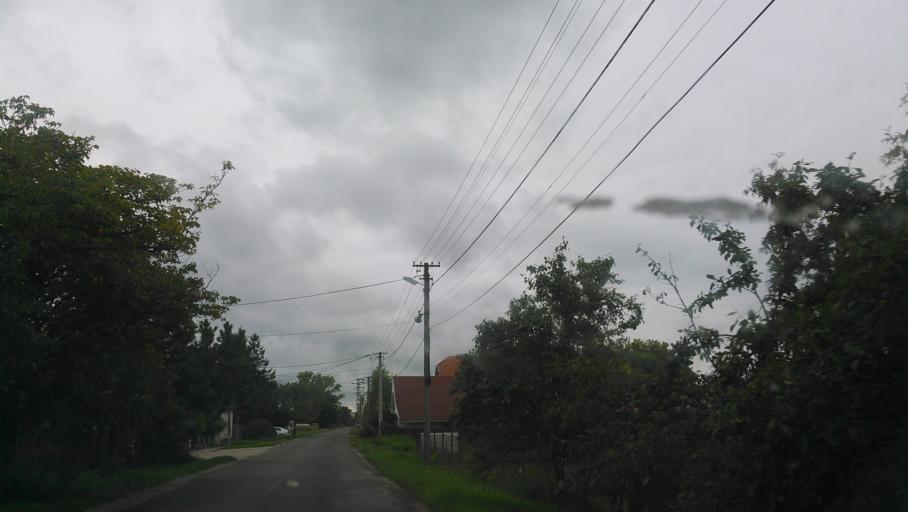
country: SK
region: Trnavsky
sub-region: Okres Dunajska Streda
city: Velky Meder
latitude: 47.8931
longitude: 17.8018
